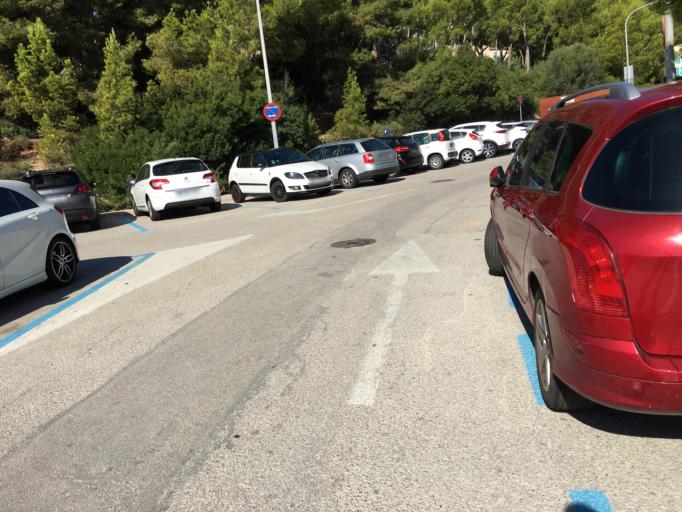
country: ES
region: Balearic Islands
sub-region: Illes Balears
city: Magaluf
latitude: 39.5341
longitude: 2.5893
